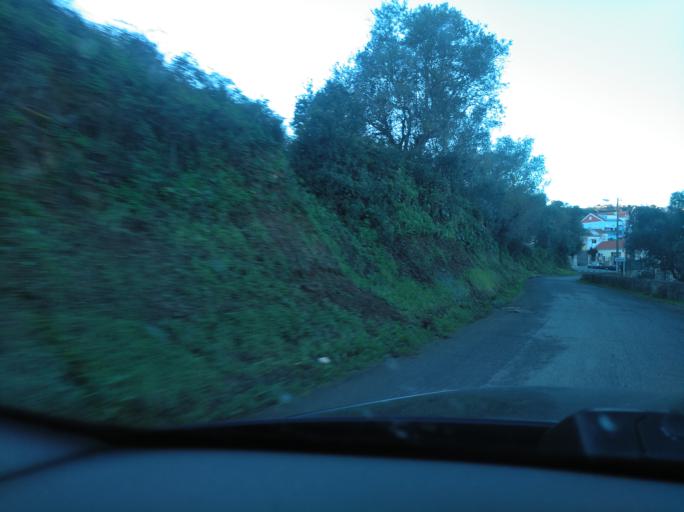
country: PT
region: Lisbon
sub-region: Loures
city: Unhos
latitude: 38.8235
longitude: -9.1209
